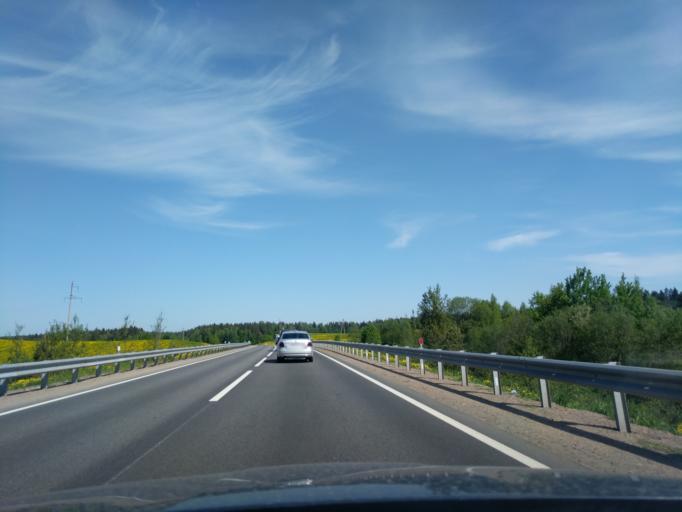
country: BY
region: Minsk
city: Bal'shavik
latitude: 54.0973
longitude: 27.5351
